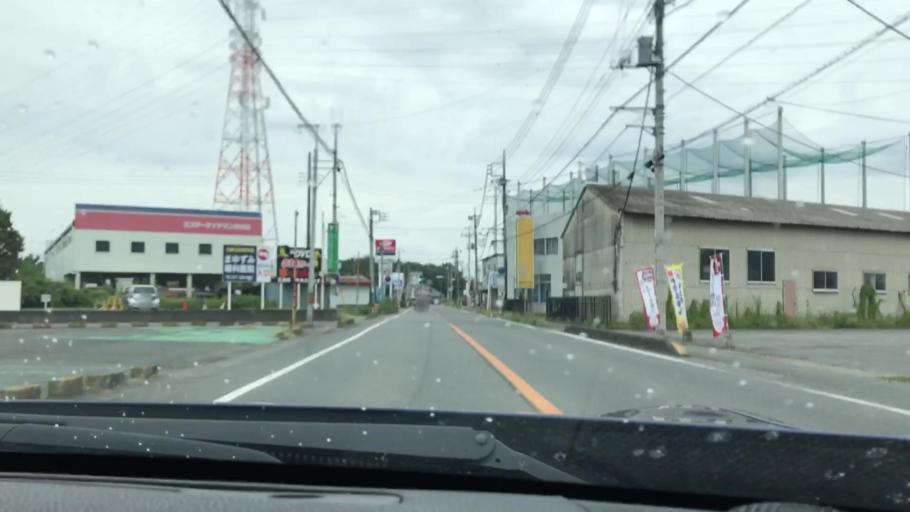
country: JP
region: Gunma
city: Takasaki
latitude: 36.3608
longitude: 139.0310
